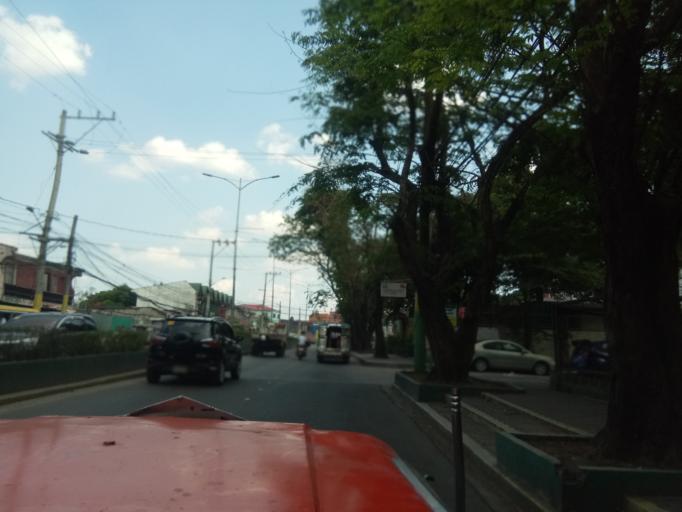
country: PH
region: Calabarzon
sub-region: Province of Cavite
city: Dasmarinas
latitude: 14.3241
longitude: 120.9629
